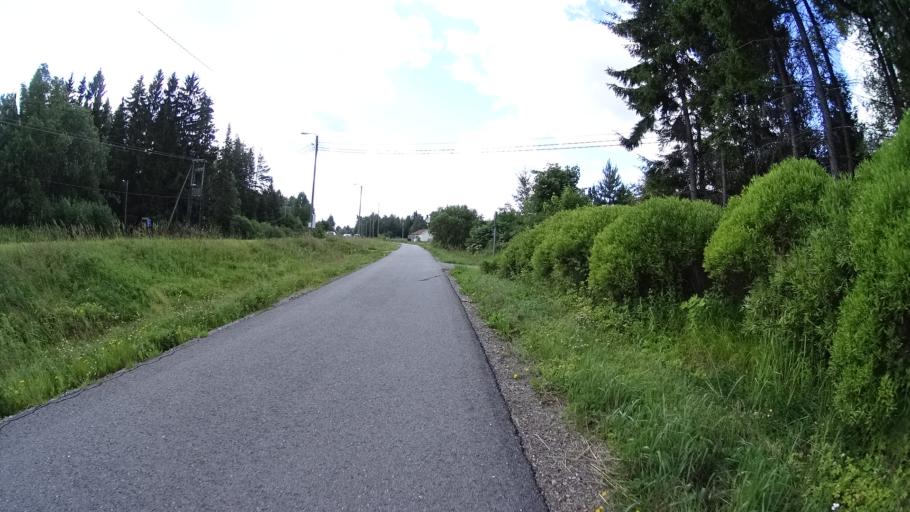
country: FI
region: Uusimaa
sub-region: Helsinki
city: Tuusula
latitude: 60.4296
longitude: 25.0548
